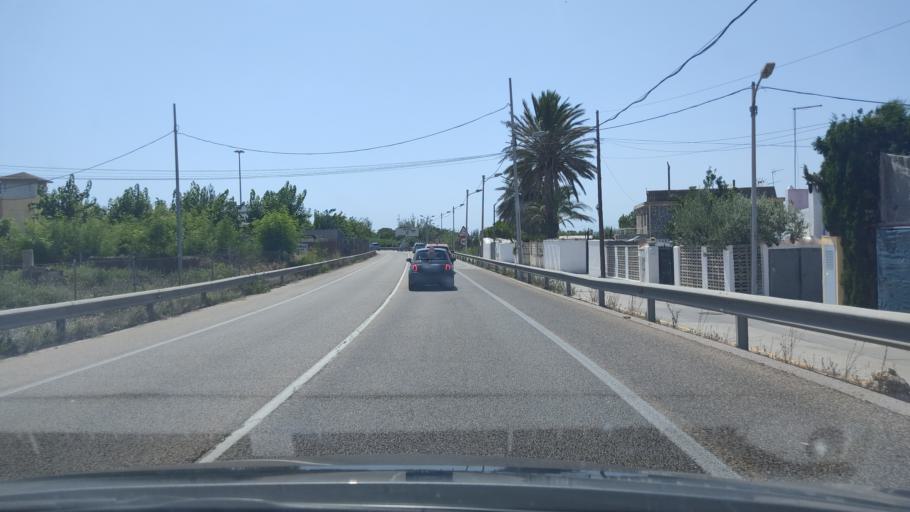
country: ES
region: Valencia
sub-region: Provincia de Valencia
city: Sollana
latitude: 39.3085
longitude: -0.2993
